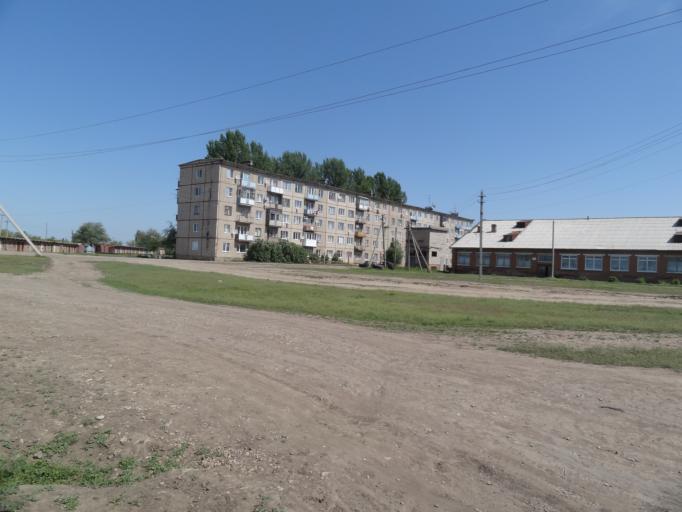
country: RU
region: Saratov
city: Engel's
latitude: 51.3733
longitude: 46.2144
